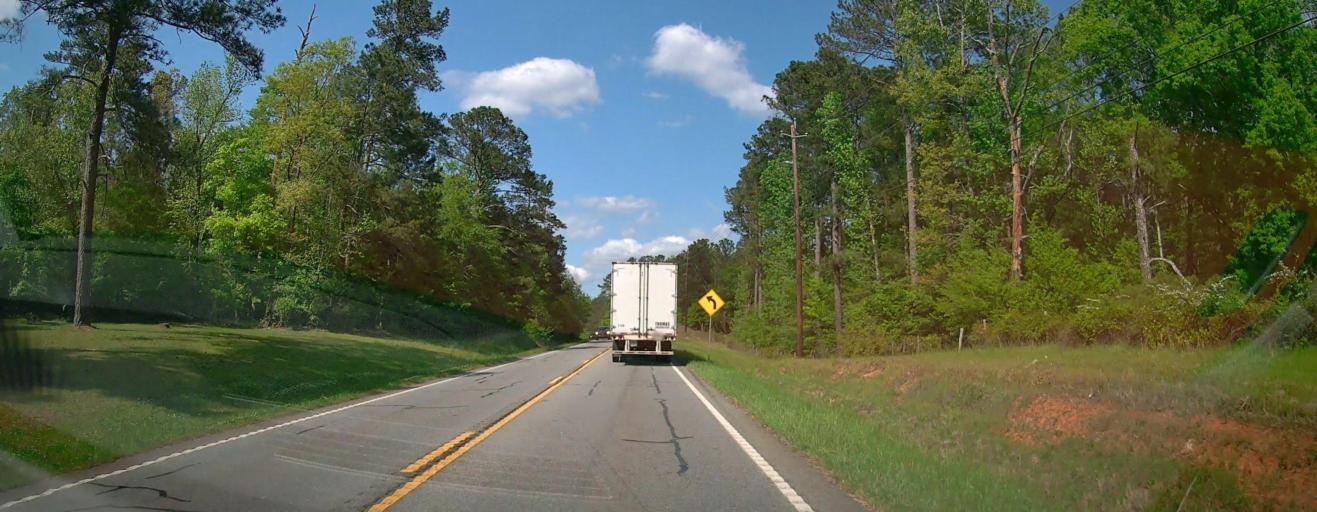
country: US
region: Georgia
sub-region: Greene County
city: Greensboro
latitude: 33.5170
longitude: -83.2244
